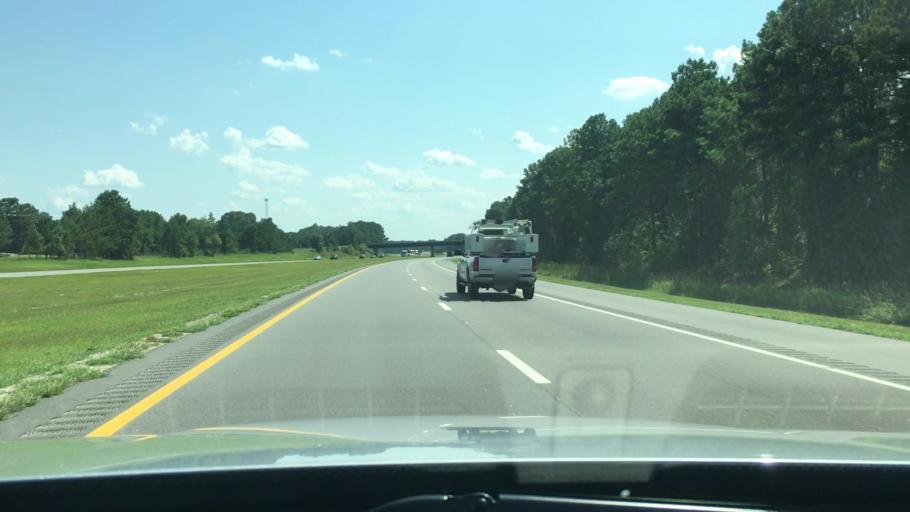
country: US
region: North Carolina
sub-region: Cumberland County
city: Vander
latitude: 35.0574
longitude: -78.7963
